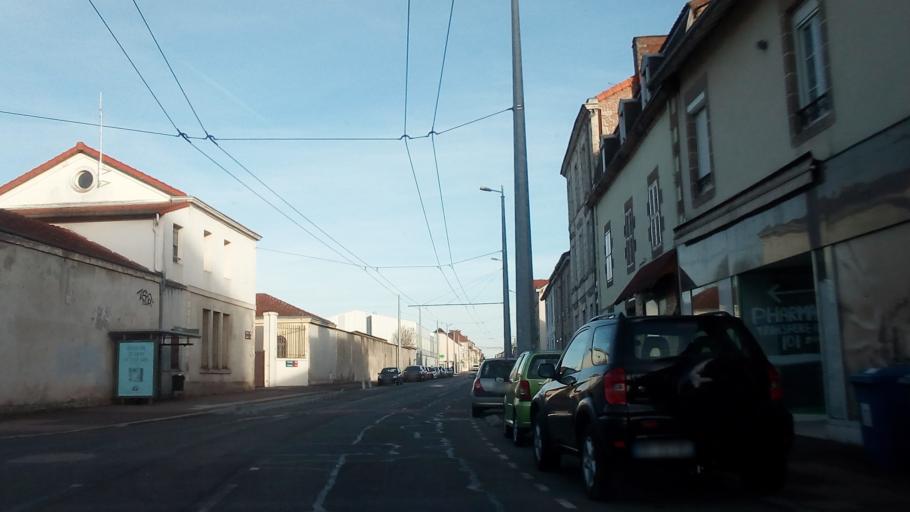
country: FR
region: Limousin
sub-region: Departement de la Haute-Vienne
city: Limoges
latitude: 45.8426
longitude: 1.2457
